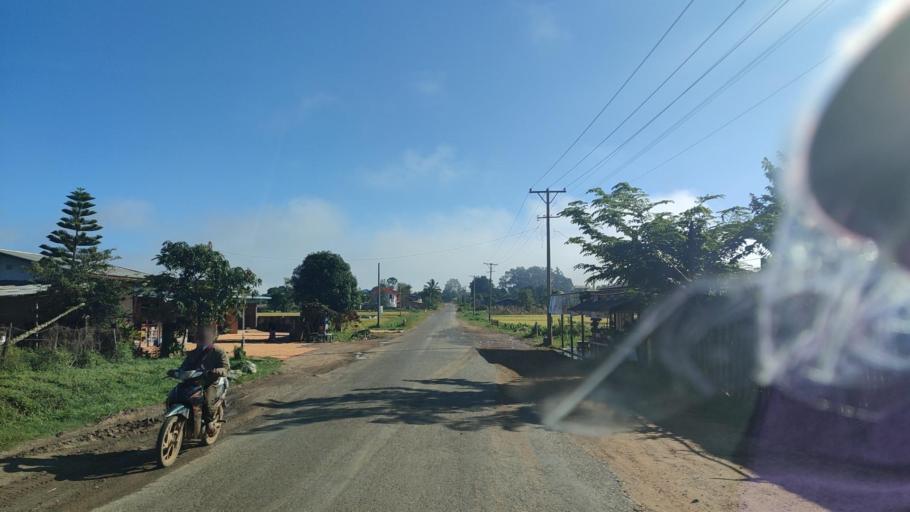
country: MM
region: Shan
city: Taunggyi
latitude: 20.9264
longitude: 97.6550
